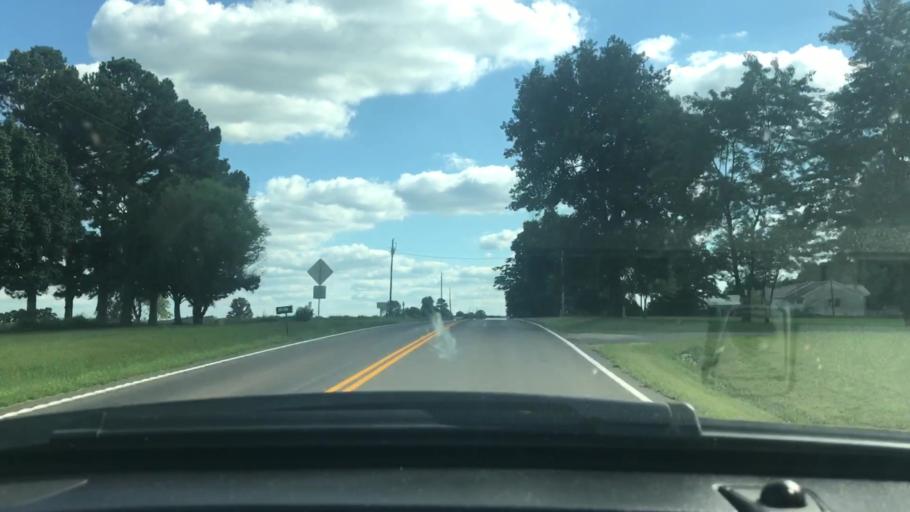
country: US
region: Missouri
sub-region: Wright County
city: Mountain Grove
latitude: 37.2515
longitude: -92.3003
